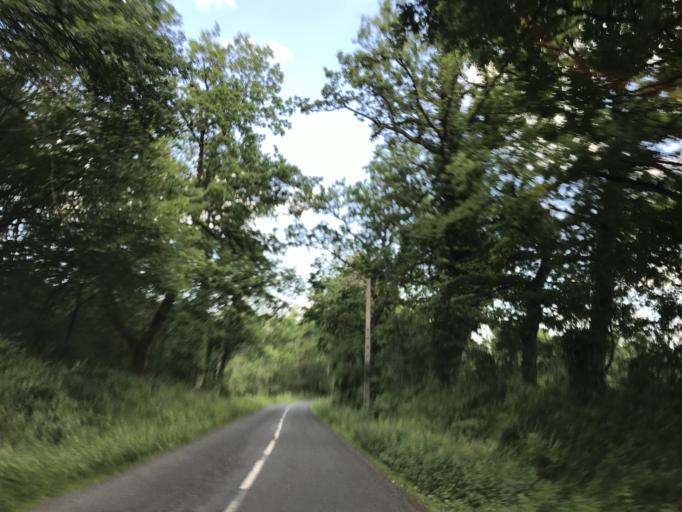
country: FR
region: Auvergne
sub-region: Departement du Puy-de-Dome
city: Courpiere
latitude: 45.7709
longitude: 3.5992
